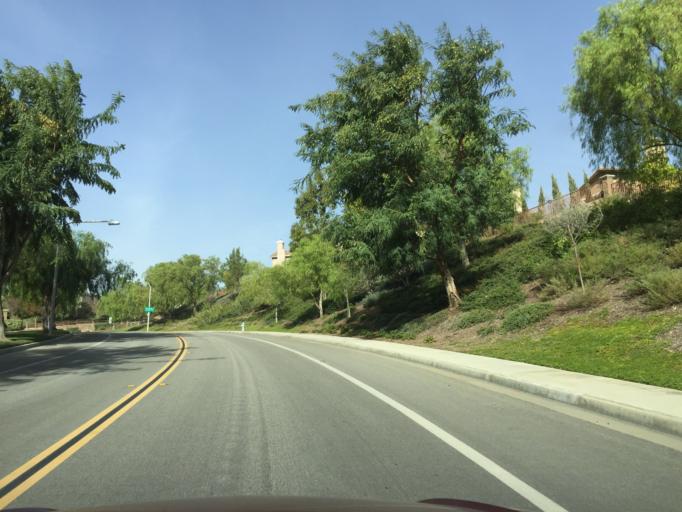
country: US
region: California
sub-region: Orange County
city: Yorba Linda
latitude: 33.9250
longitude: -117.8364
